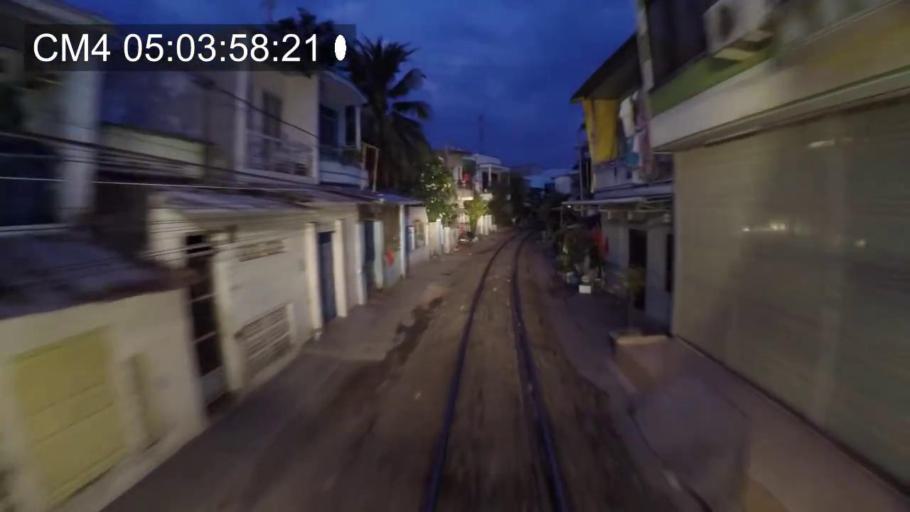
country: VN
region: Khanh Hoa
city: Nha Trang
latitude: 12.2603
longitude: 109.1717
